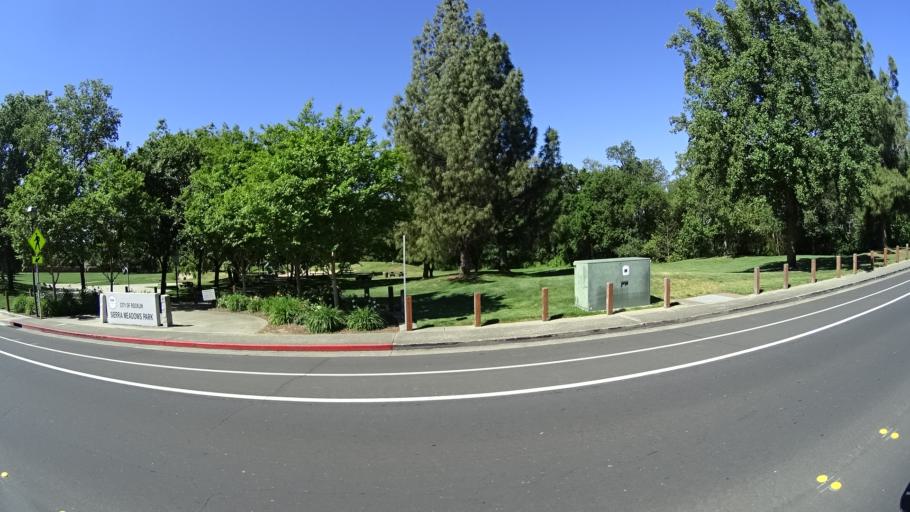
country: US
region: California
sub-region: Placer County
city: Rocklin
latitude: 38.7953
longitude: -121.2228
